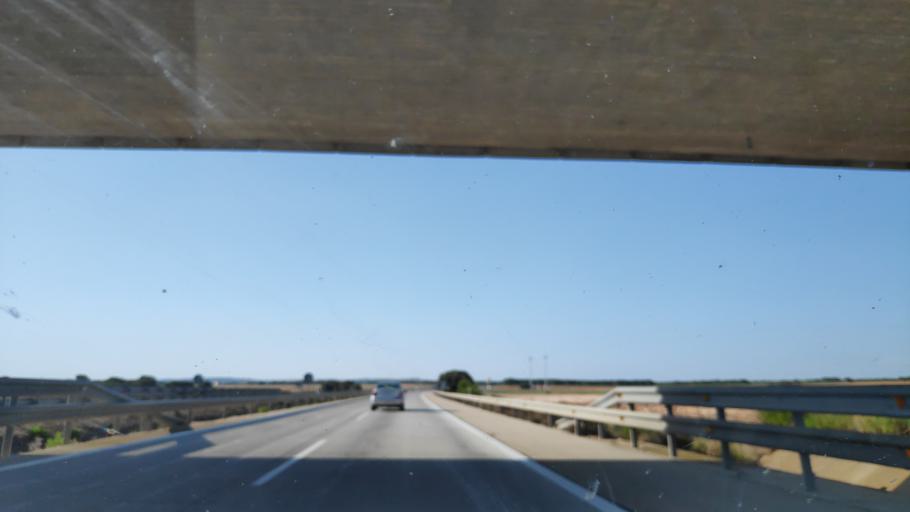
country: ES
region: Castille-La Mancha
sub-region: Provincia de Cuenca
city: Casas de Guijarro
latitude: 39.3151
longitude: -2.2035
